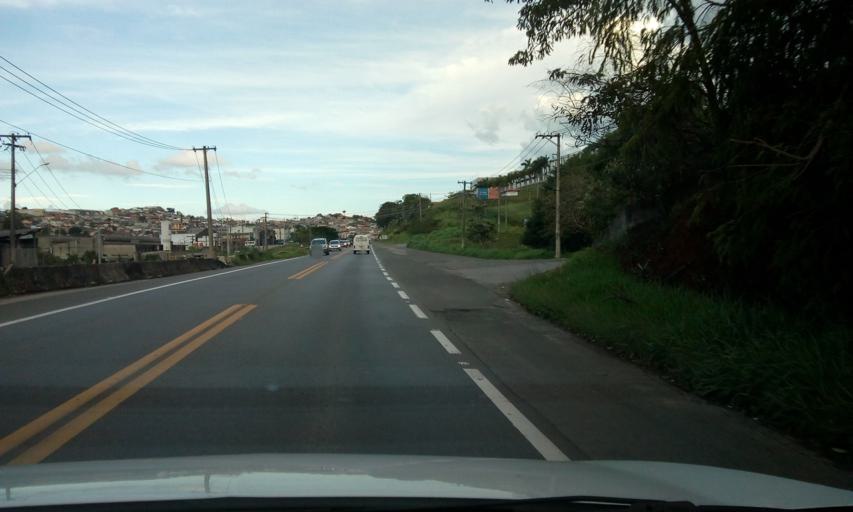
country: BR
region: Sao Paulo
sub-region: Itatiba
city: Itatiba
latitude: -23.0142
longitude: -46.8343
